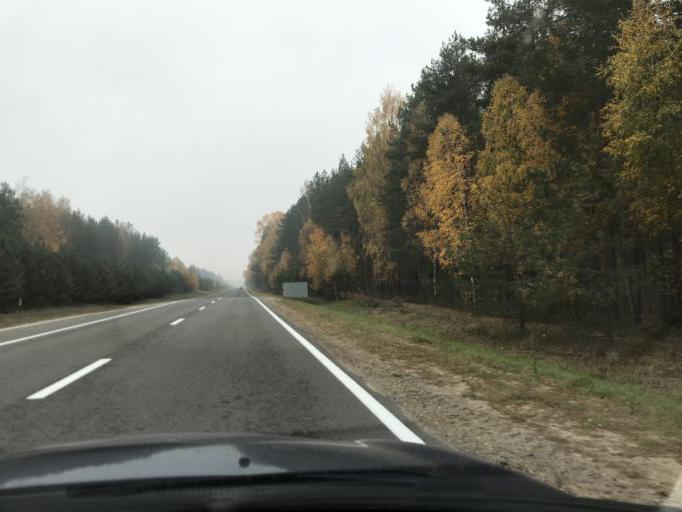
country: LT
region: Alytaus apskritis
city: Druskininkai
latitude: 53.9047
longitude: 23.9179
